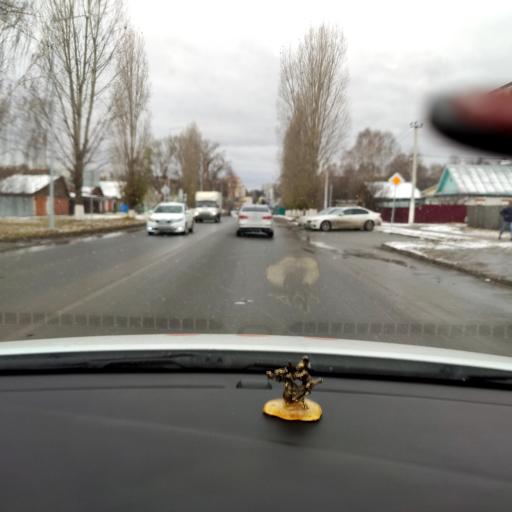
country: RU
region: Tatarstan
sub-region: Zelenodol'skiy Rayon
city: Zelenodolsk
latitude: 55.8479
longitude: 48.5289
